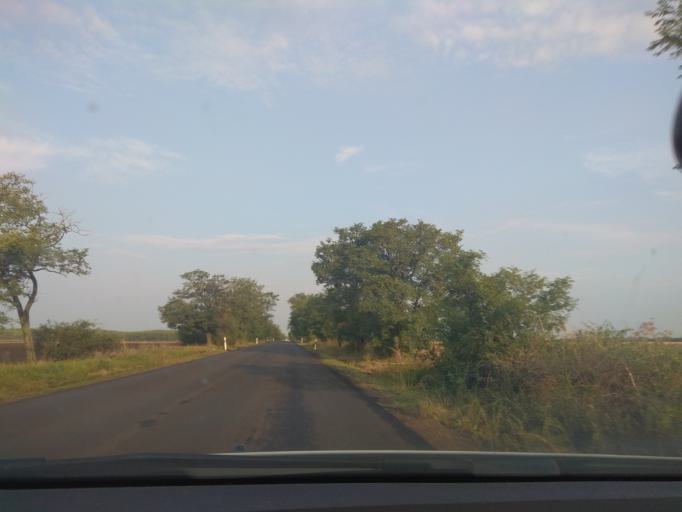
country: HU
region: Heves
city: Szihalom
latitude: 47.8163
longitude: 20.5162
